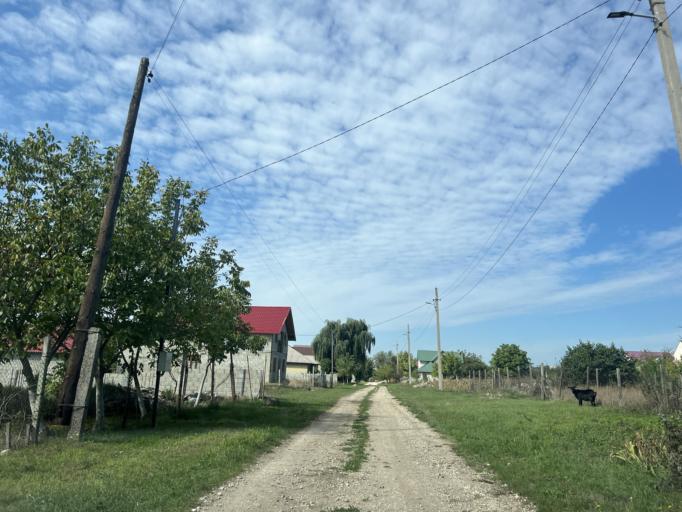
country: MD
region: Ungheni
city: Ungheni
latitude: 47.2012
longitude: 27.8179
